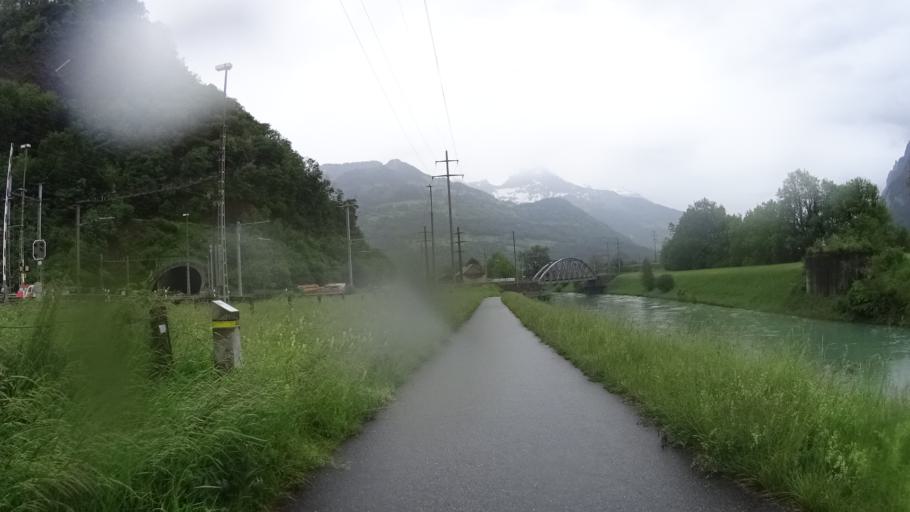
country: CH
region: Glarus
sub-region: Glarus
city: Niederurnen
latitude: 47.1330
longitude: 9.0647
